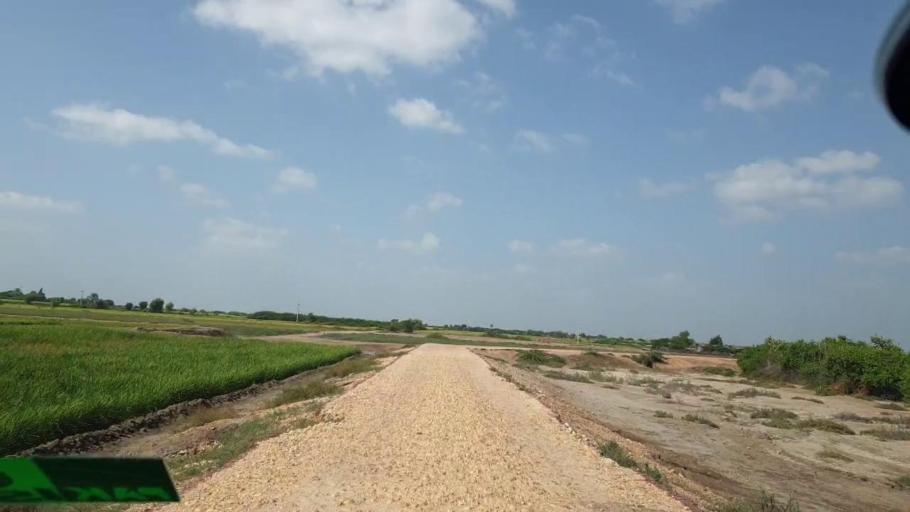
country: PK
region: Sindh
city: Tando Bago
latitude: 24.6656
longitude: 69.2039
